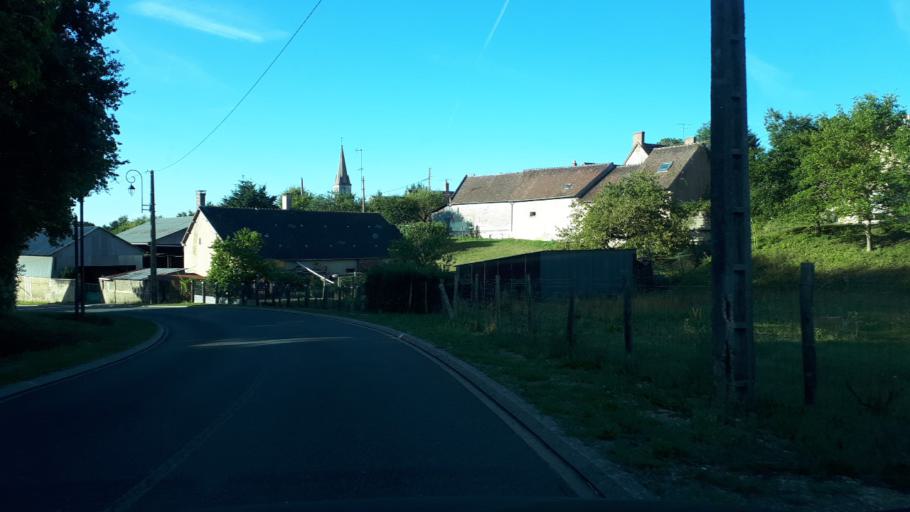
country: FR
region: Centre
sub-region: Departement du Loir-et-Cher
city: Lunay
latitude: 47.7549
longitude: 0.9382
